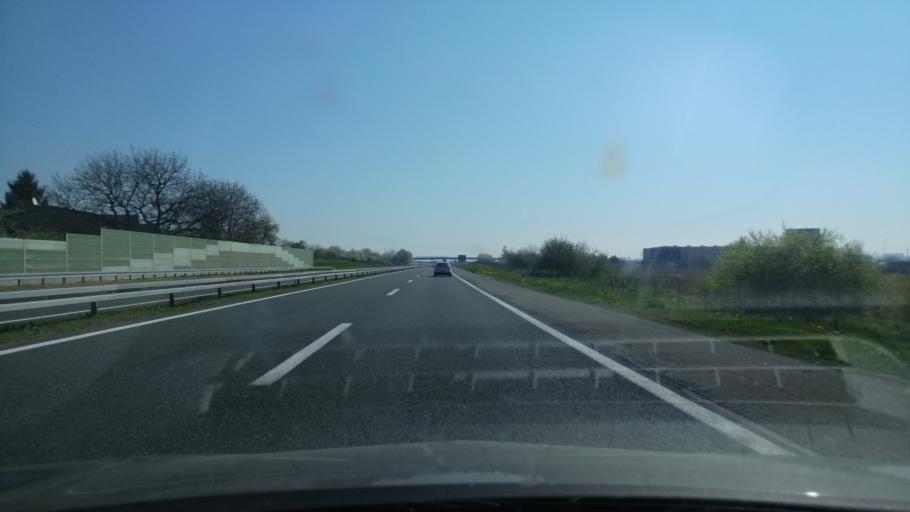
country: HR
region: Brodsko-Posavska
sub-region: Grad Slavonski Brod
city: Slavonski Brod
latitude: 45.1801
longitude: 17.9843
